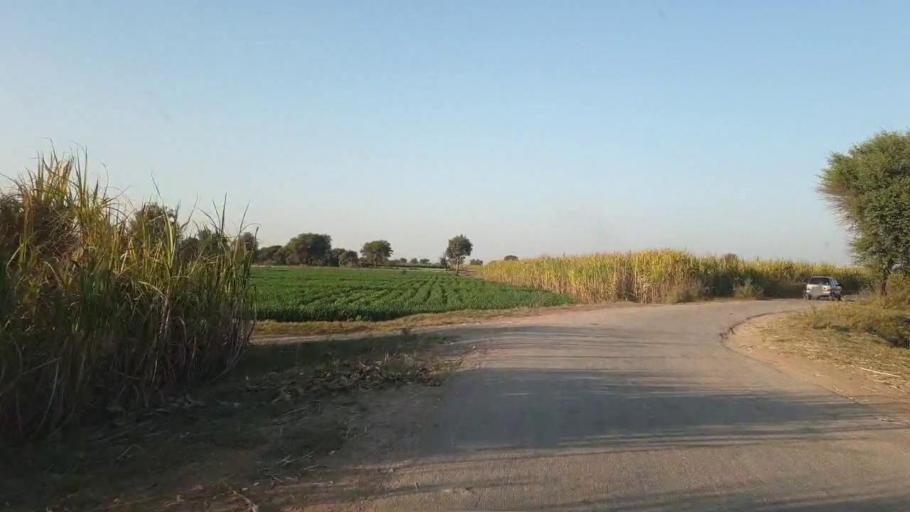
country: PK
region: Sindh
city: Chambar
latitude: 25.3618
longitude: 68.7400
